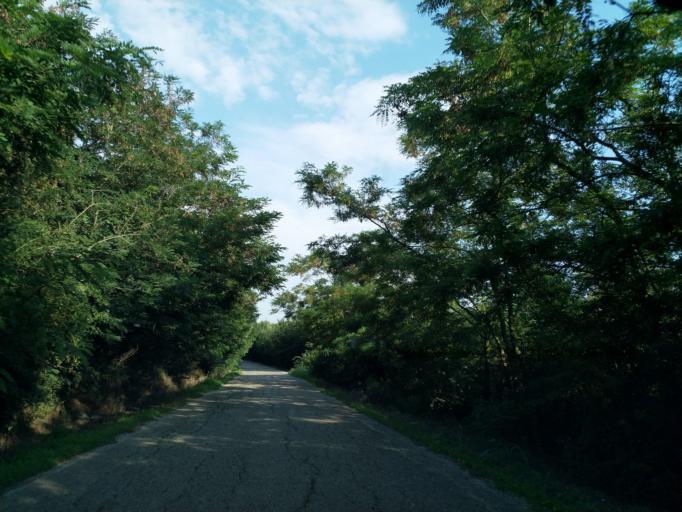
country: RS
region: Central Serbia
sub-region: Pomoravski Okrug
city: Jagodina
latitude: 43.9961
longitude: 21.1938
